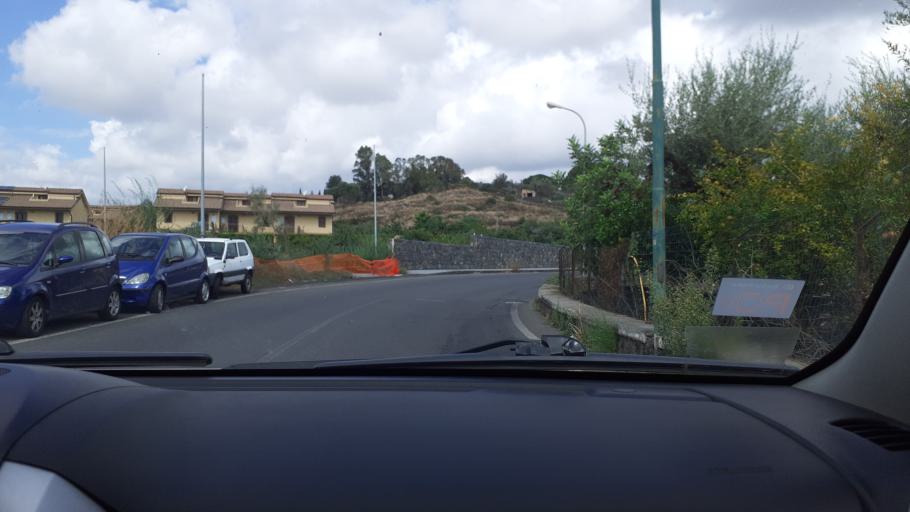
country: IT
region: Sicily
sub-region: Catania
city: Carrubazza-Motta
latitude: 37.5568
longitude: 15.1090
